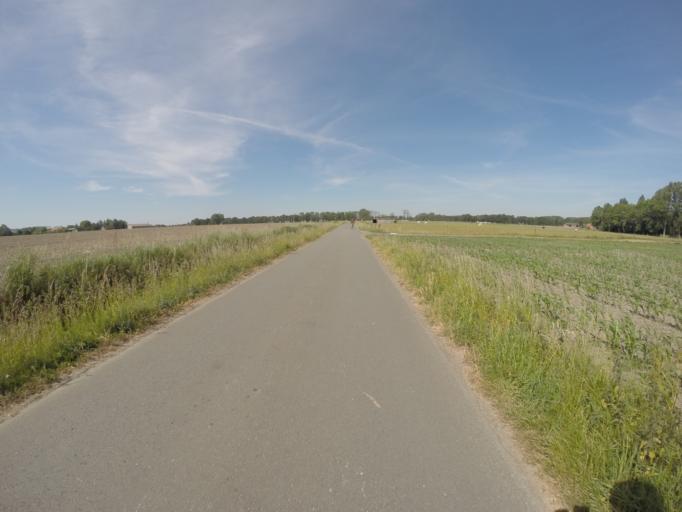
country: BE
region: Flanders
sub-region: Provincie West-Vlaanderen
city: Beernem
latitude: 51.1840
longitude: 3.3476
